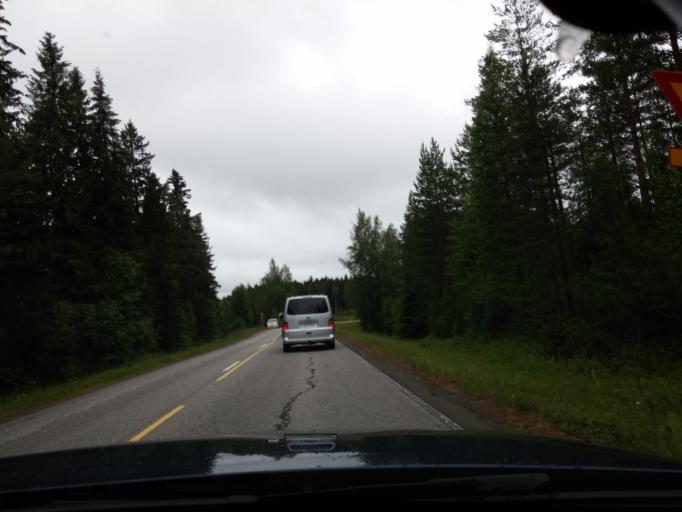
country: FI
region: Central Finland
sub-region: Keuruu
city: Multia
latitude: 62.4203
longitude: 24.7777
